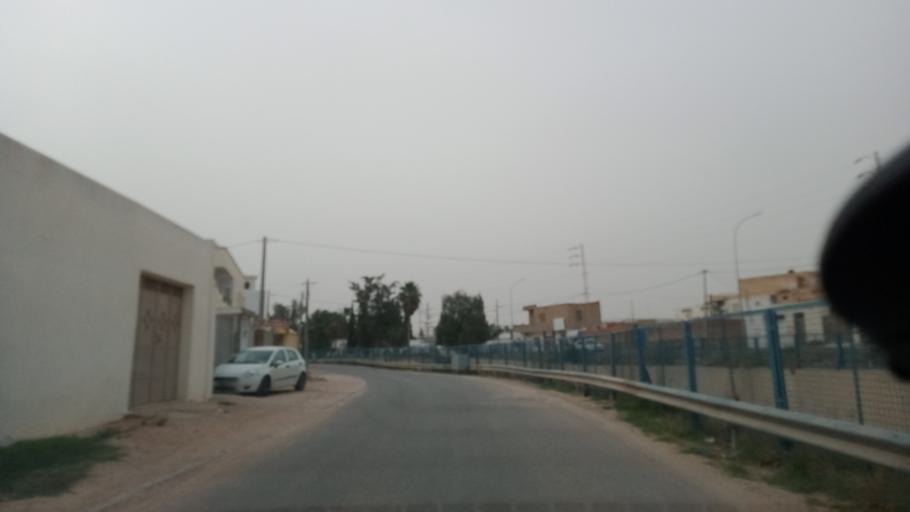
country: TN
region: Safaqis
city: Al Qarmadah
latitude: 34.7969
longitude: 10.7722
